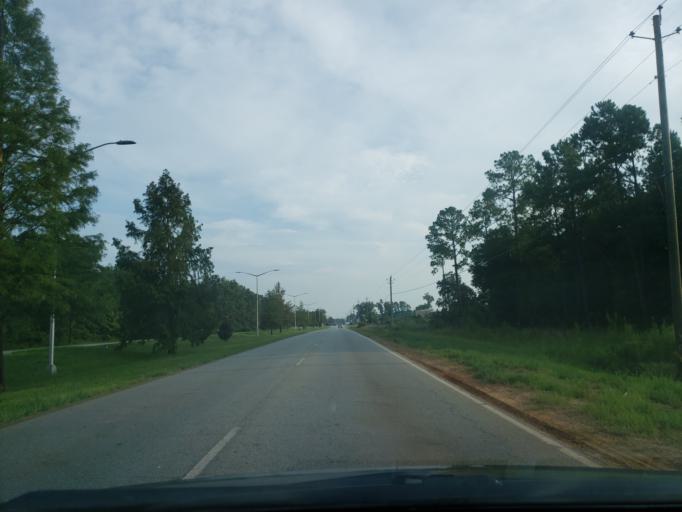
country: US
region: Georgia
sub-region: Dougherty County
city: Albany
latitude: 31.5814
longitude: -84.2193
